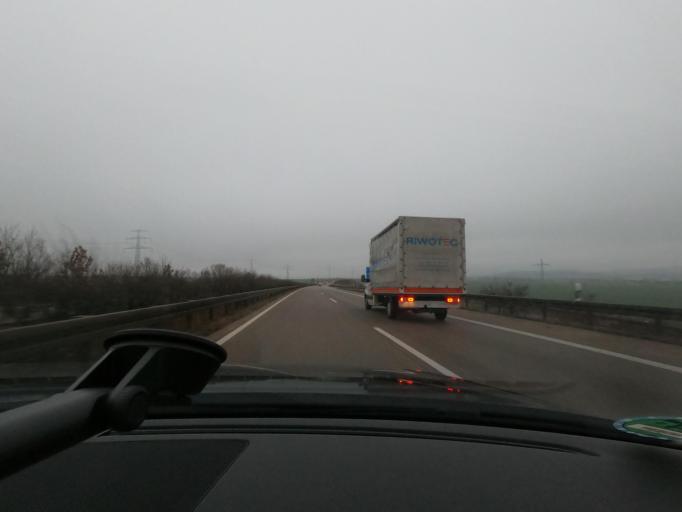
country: DE
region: Thuringia
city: Alkersleben
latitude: 50.8509
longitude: 11.0098
